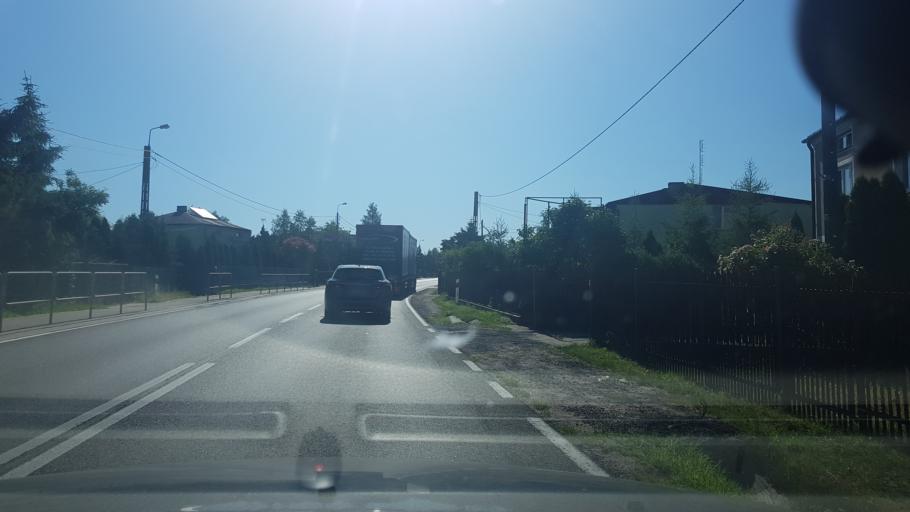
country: PL
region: Masovian Voivodeship
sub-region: Powiat wegrowski
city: Lochow
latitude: 52.5397
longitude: 21.6623
